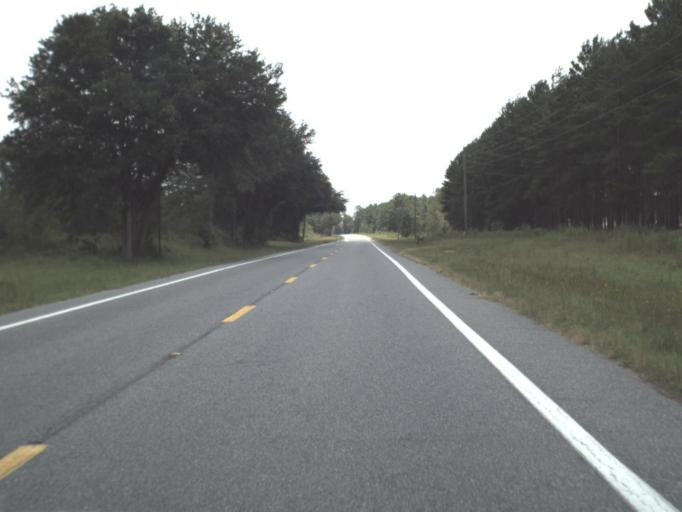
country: US
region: Florida
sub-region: Madison County
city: Madison
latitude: 30.4866
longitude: -83.1906
